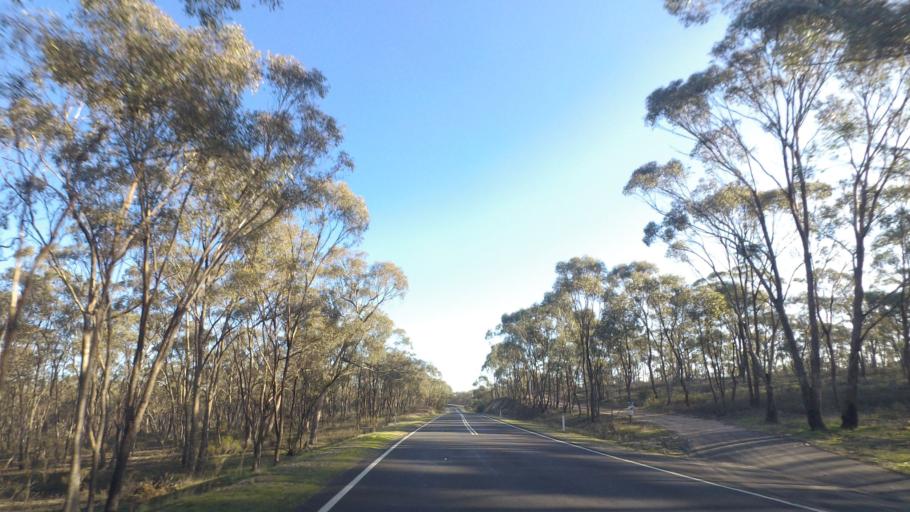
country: AU
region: Victoria
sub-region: Greater Bendigo
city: Kennington
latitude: -36.8739
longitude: 144.4972
